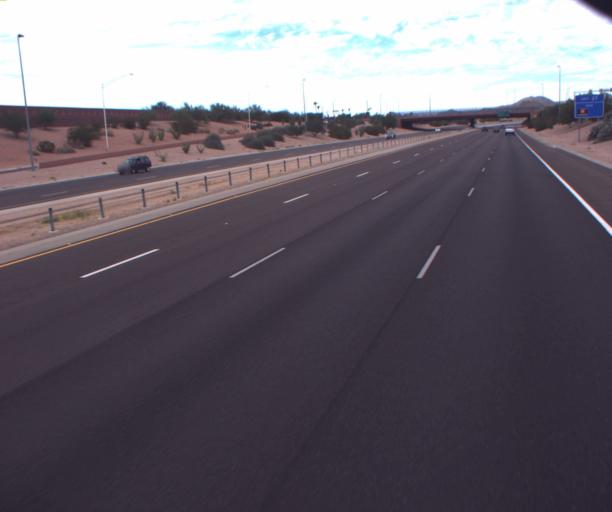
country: US
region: Arizona
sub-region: Pinal County
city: Apache Junction
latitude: 33.4046
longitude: -111.6399
